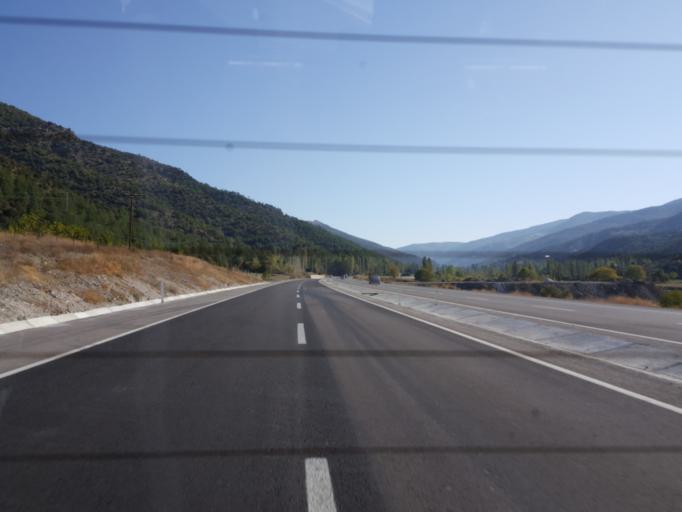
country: TR
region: Tokat
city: Turhal
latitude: 40.4717
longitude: 36.1309
